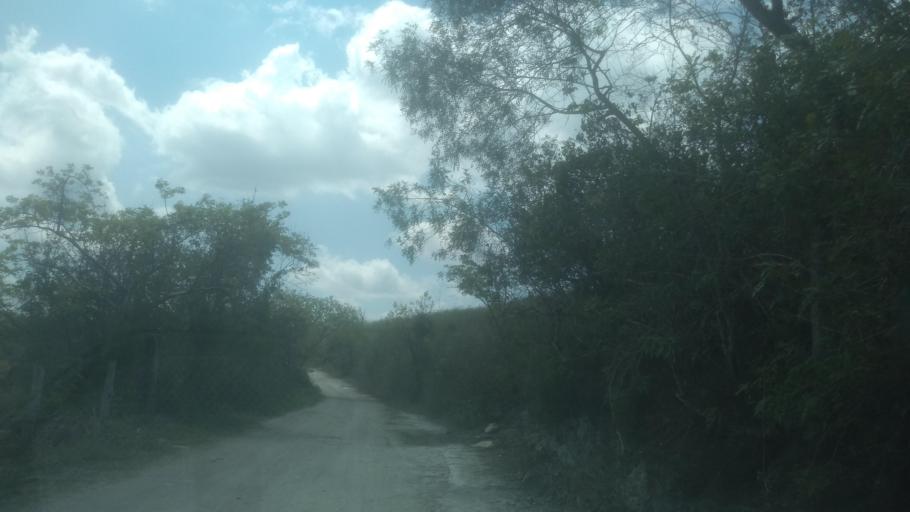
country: MX
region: Veracruz
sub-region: Emiliano Zapata
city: Plan del Rio
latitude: 19.3976
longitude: -96.6370
